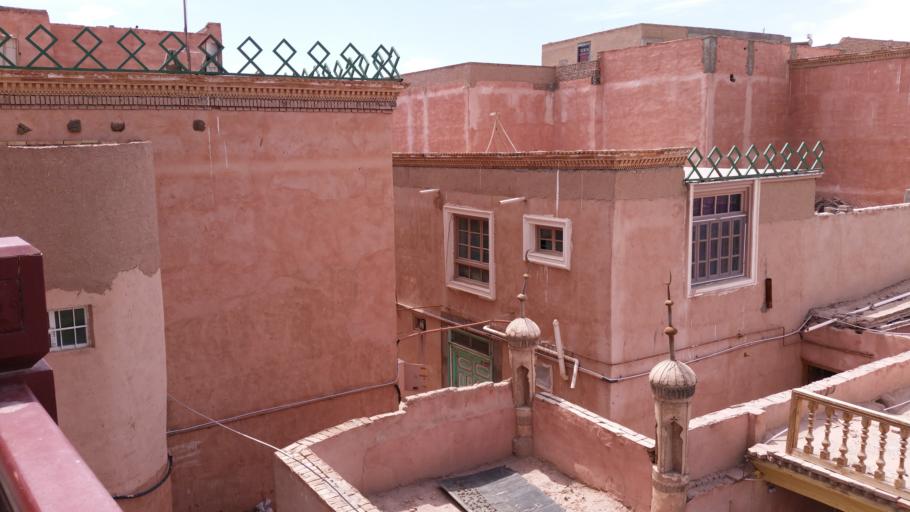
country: CN
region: Xinjiang Uygur Zizhiqu
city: Kashi
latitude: 39.4742
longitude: 75.9937
